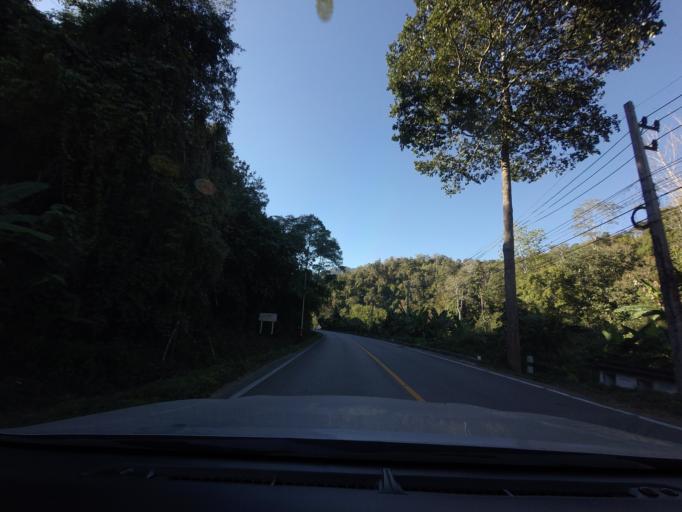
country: TH
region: Mae Hong Son
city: Mae Hi
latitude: 19.2042
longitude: 98.6784
